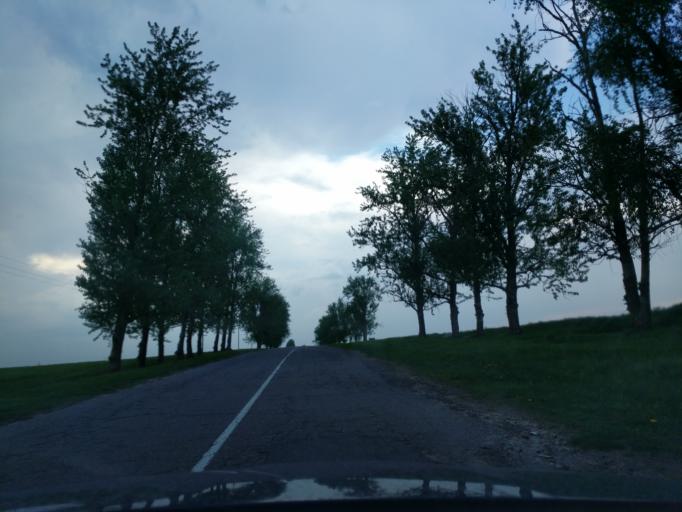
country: BY
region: Minsk
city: Novy Svyerzhan'
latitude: 53.4761
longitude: 26.6319
